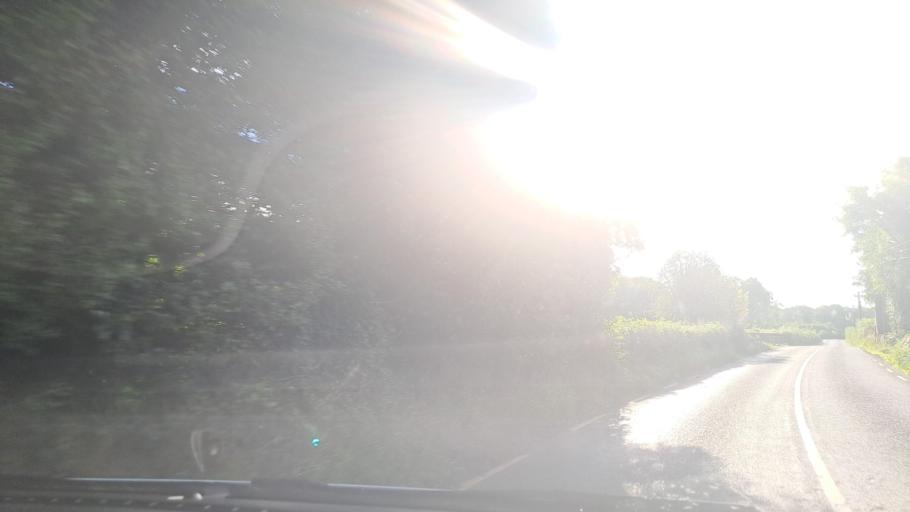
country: IE
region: Ulster
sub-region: County Monaghan
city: Carrickmacross
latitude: 53.9886
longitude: -6.7662
